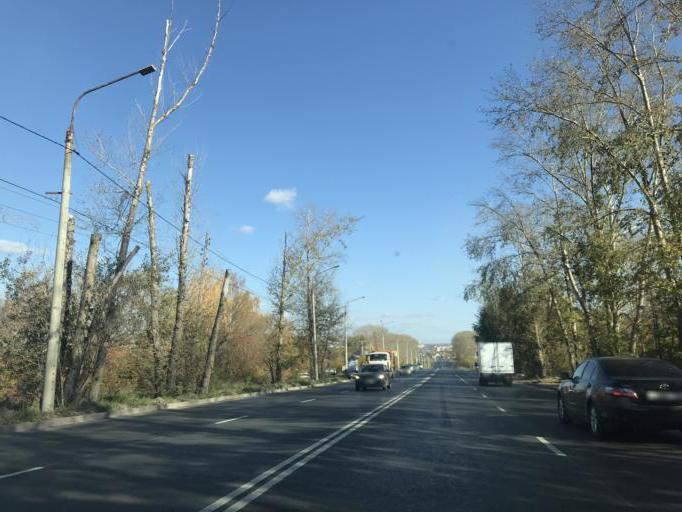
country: RU
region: Chelyabinsk
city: Roshchino
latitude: 55.2406
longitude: 61.3312
